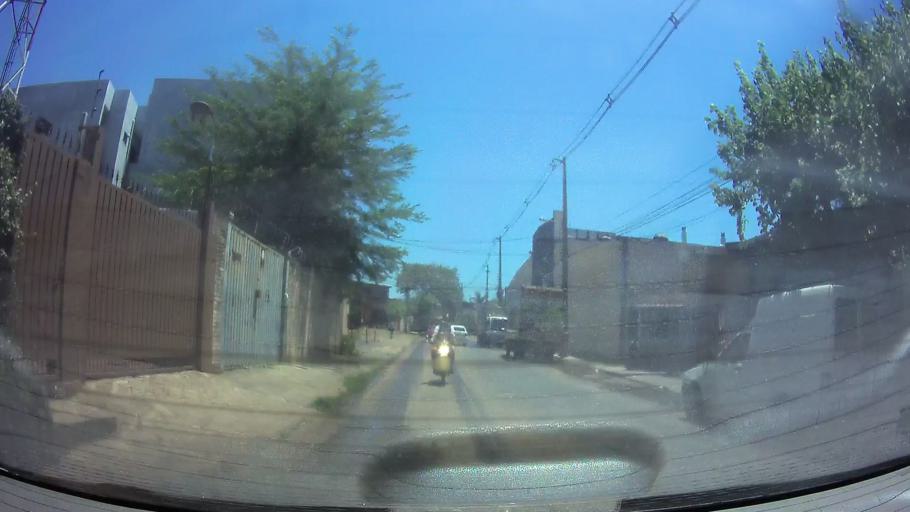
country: PY
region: Central
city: San Lorenzo
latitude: -25.3417
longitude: -57.4888
